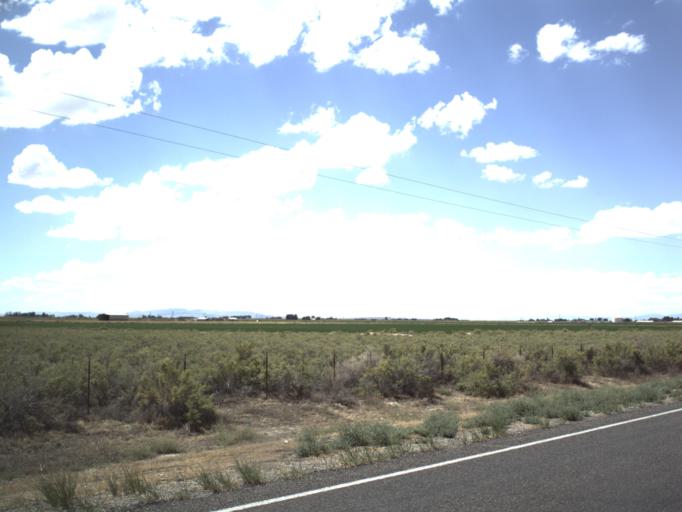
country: US
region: Utah
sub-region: Millard County
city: Delta
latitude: 39.3530
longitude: -112.5291
